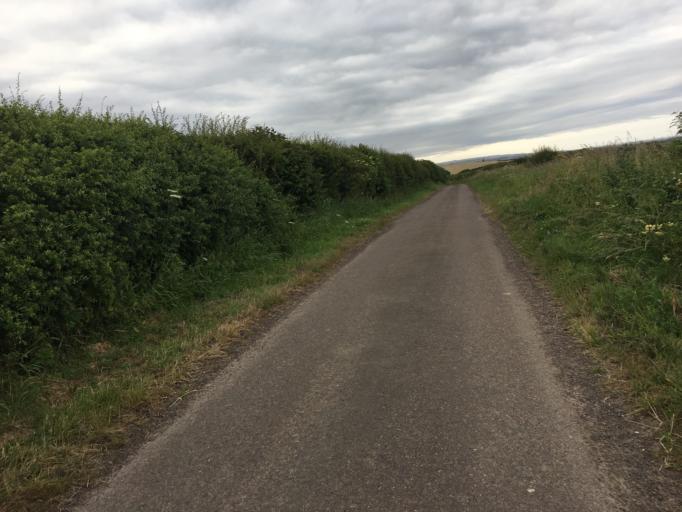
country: GB
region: England
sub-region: Northumberland
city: Lowick
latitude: 55.6562
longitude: -1.9030
